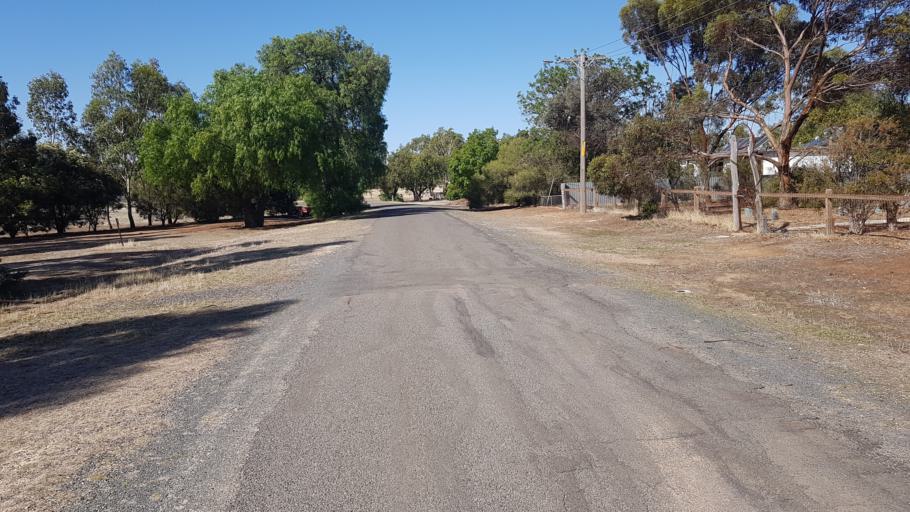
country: AU
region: Victoria
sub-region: Horsham
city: Horsham
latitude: -36.7447
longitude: 141.9419
